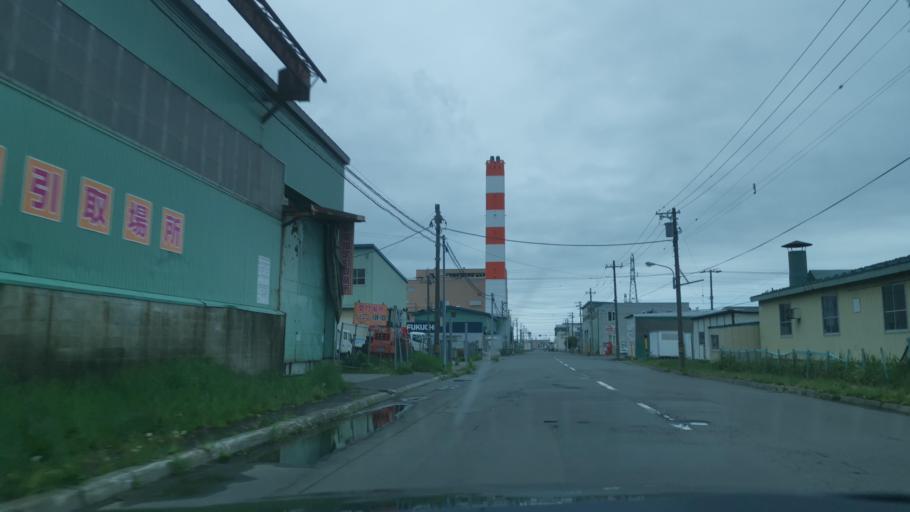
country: JP
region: Hokkaido
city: Sapporo
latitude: 43.1075
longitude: 141.2865
